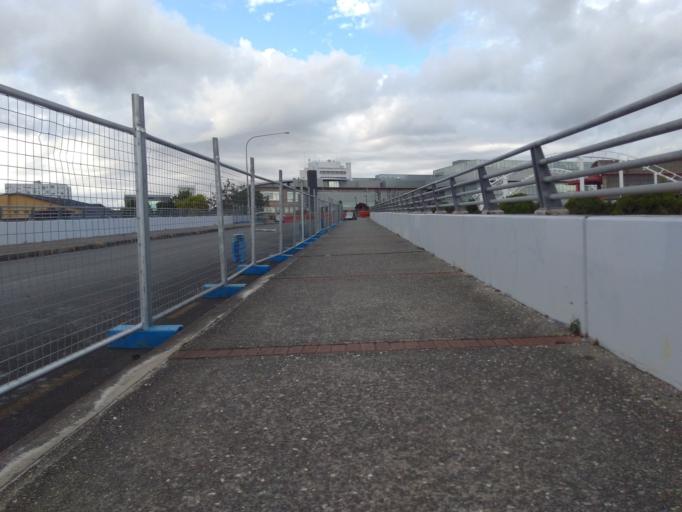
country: NZ
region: Auckland
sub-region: Auckland
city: Manukau City
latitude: -36.9965
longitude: 174.8816
